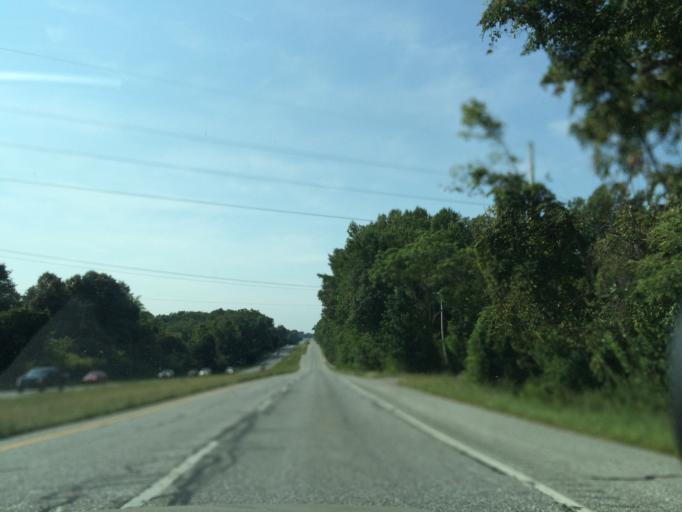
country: US
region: Virginia
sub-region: King George County
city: Dahlgren
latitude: 38.3970
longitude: -76.9538
